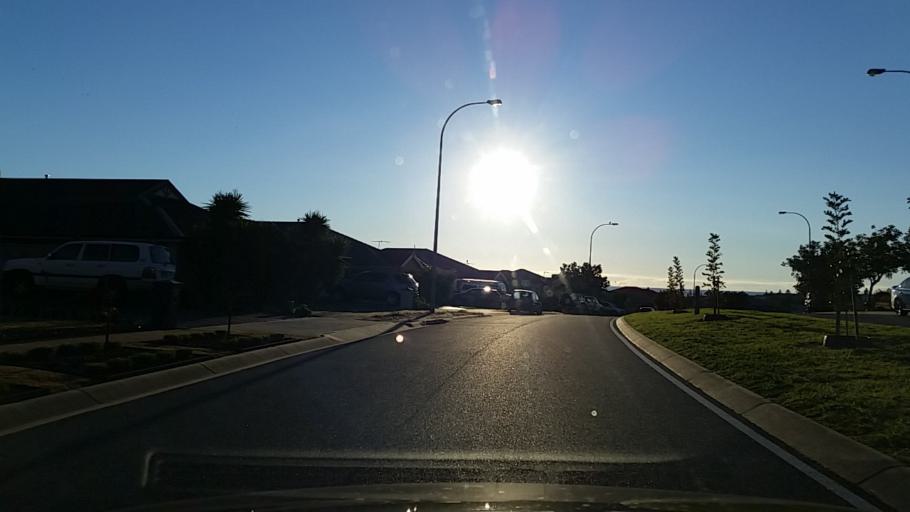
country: AU
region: South Australia
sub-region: Onkaparinga
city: Moana
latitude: -35.2097
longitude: 138.4845
